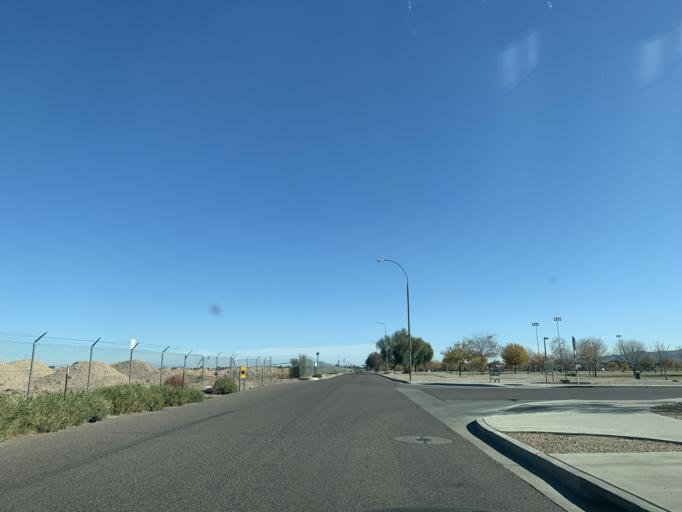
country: US
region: Arizona
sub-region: Maricopa County
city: Laveen
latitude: 33.3994
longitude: -112.1296
